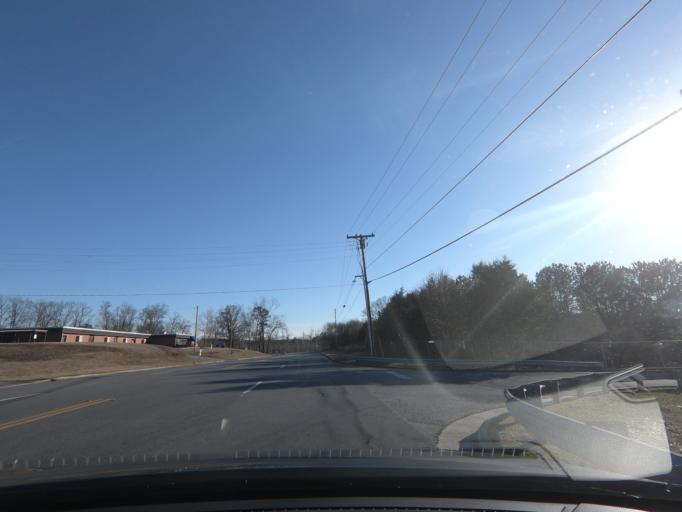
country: US
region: Georgia
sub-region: Gordon County
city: Calhoun
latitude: 34.4583
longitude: -84.9166
